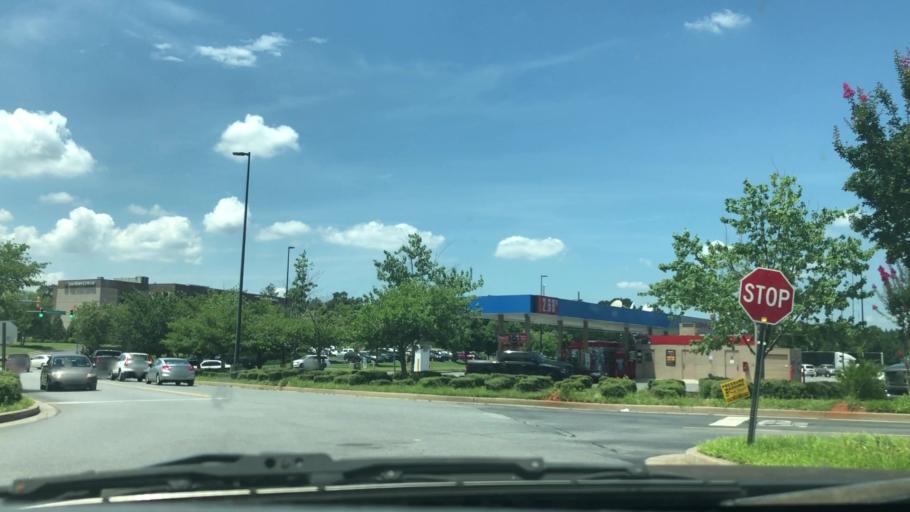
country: US
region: Georgia
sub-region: Bartow County
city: Cartersville
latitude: 34.2015
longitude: -84.7893
